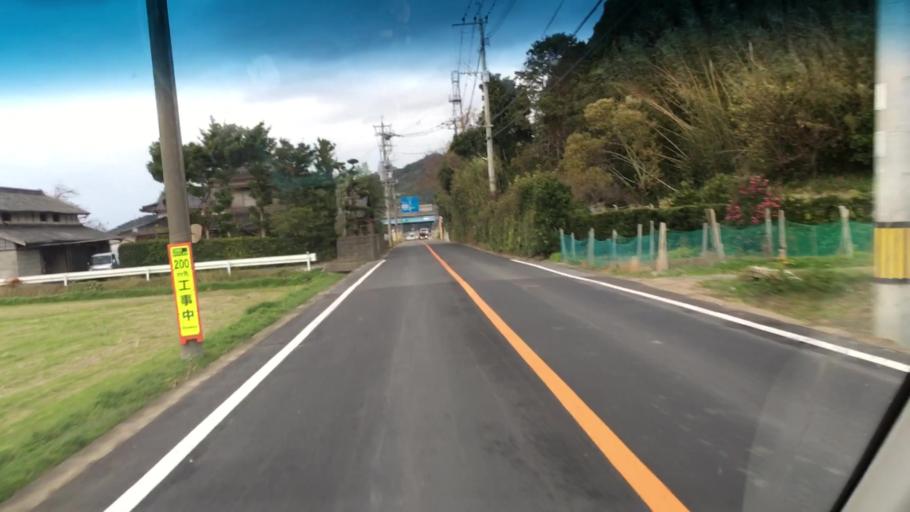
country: JP
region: Fukuoka
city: Maebaru-chuo
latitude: 33.5294
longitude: 130.1891
